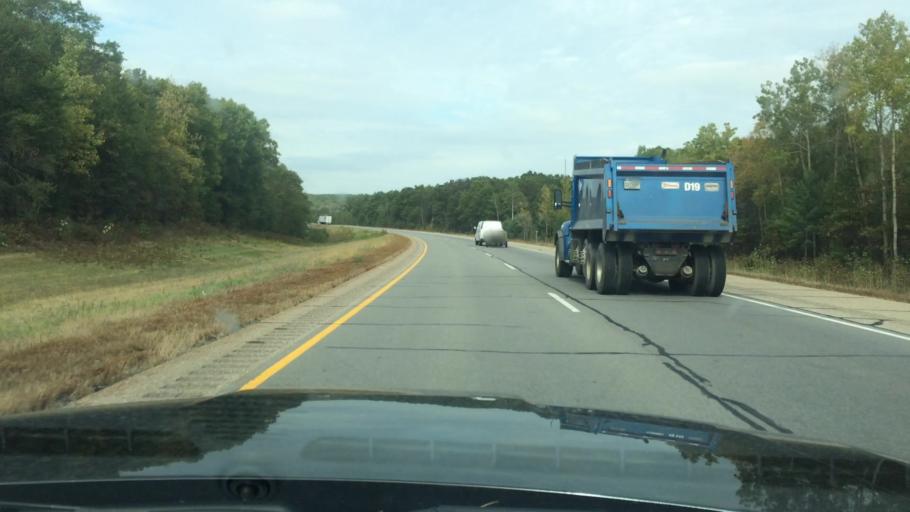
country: US
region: Wisconsin
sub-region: Marathon County
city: Mosinee
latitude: 44.6901
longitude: -89.6411
